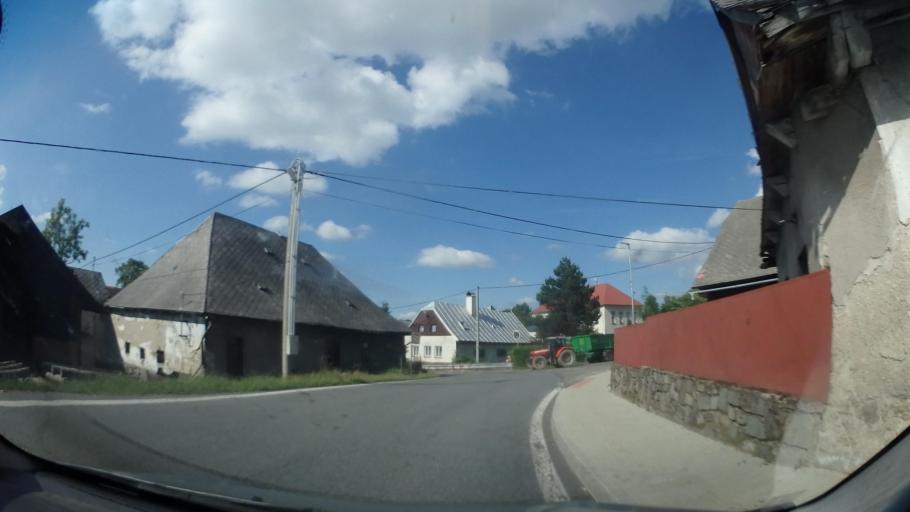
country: CZ
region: Vysocina
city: Heralec
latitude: 49.6884
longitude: 15.9927
